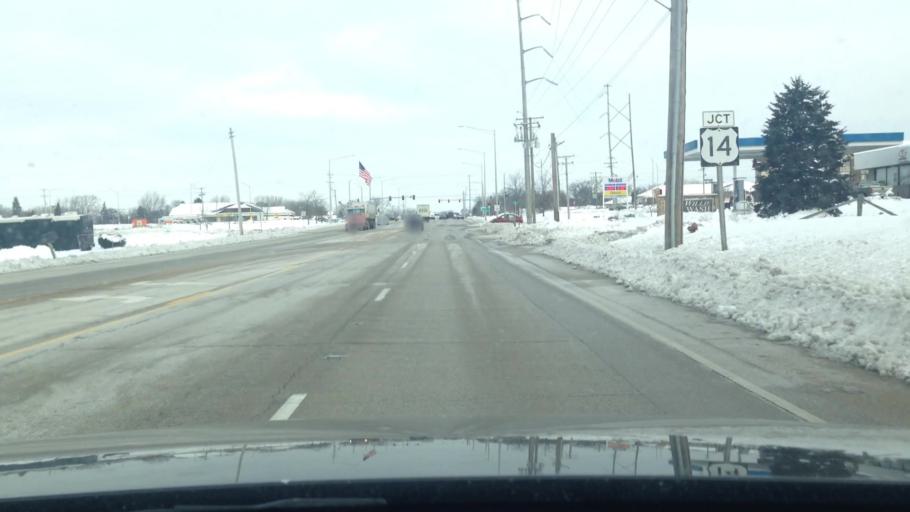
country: US
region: Illinois
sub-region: McHenry County
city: Woodstock
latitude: 42.2923
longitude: -88.4331
